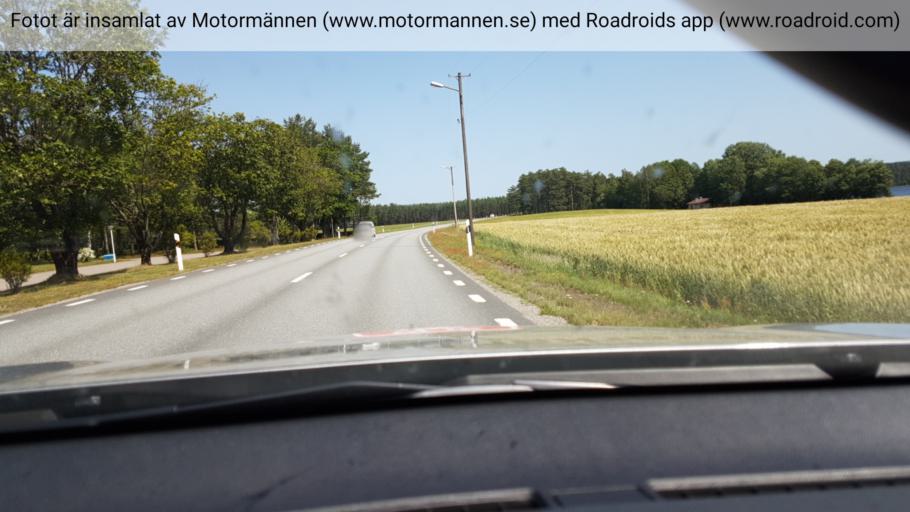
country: SE
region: Joenkoeping
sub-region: Nassjo Kommun
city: Bodafors
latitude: 57.4688
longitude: 14.7599
